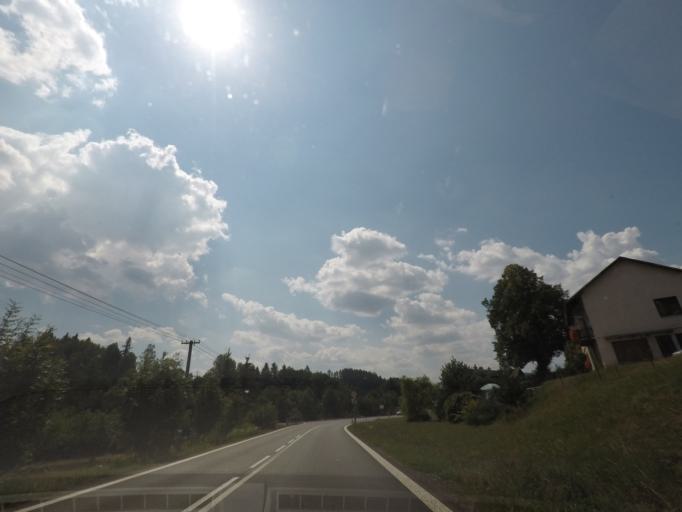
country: CZ
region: Kralovehradecky
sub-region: Okres Trutnov
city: Hostinne
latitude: 50.5198
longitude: 15.7589
